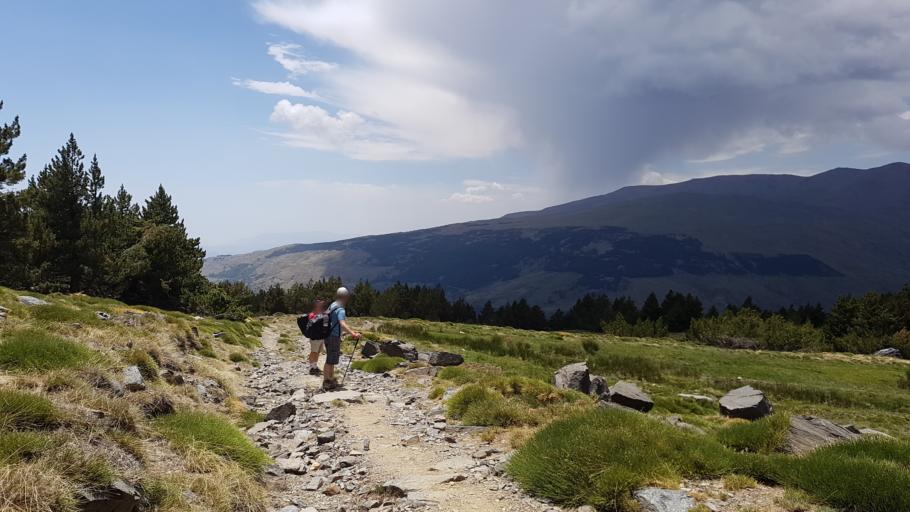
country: ES
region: Andalusia
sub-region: Provincia de Granada
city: Capileira
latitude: 36.9906
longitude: -3.3256
